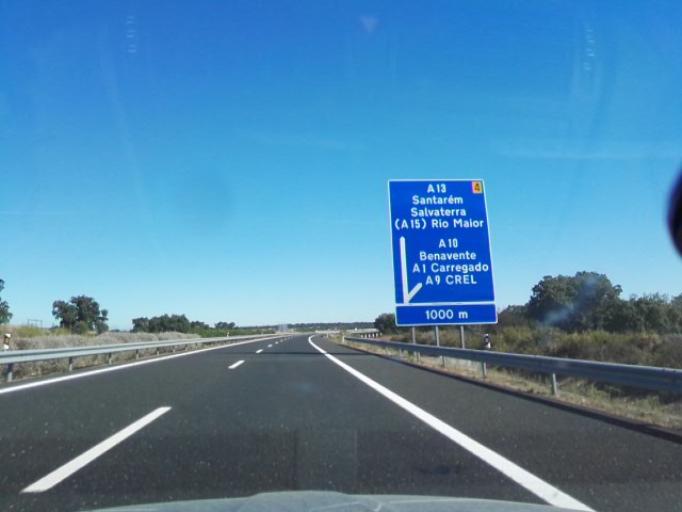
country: PT
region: Santarem
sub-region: Benavente
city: Poceirao
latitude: 38.8852
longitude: -8.7938
